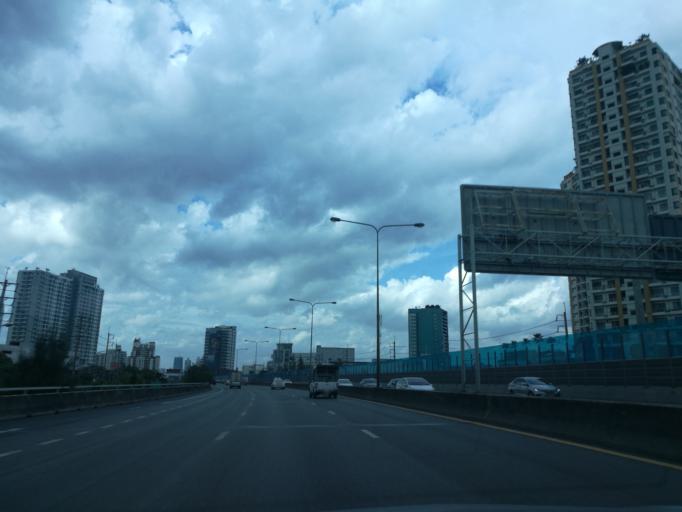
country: TH
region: Bangkok
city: Yan Nawa
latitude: 13.6976
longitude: 100.5383
